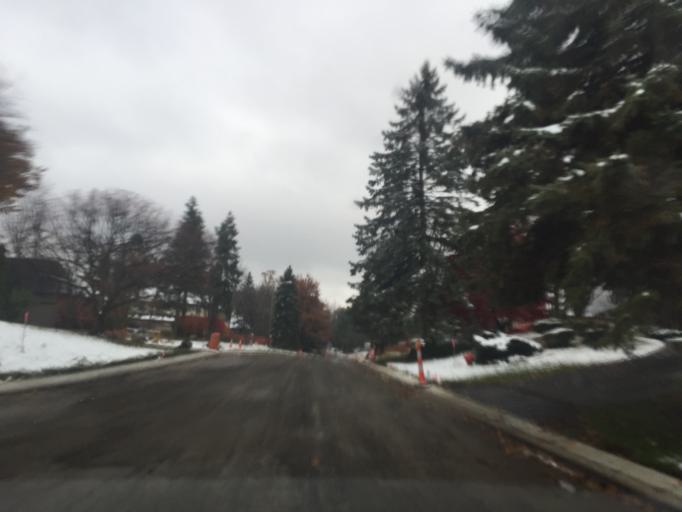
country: US
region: Michigan
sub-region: Oakland County
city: Bloomfield Hills
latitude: 42.5998
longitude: -83.2762
